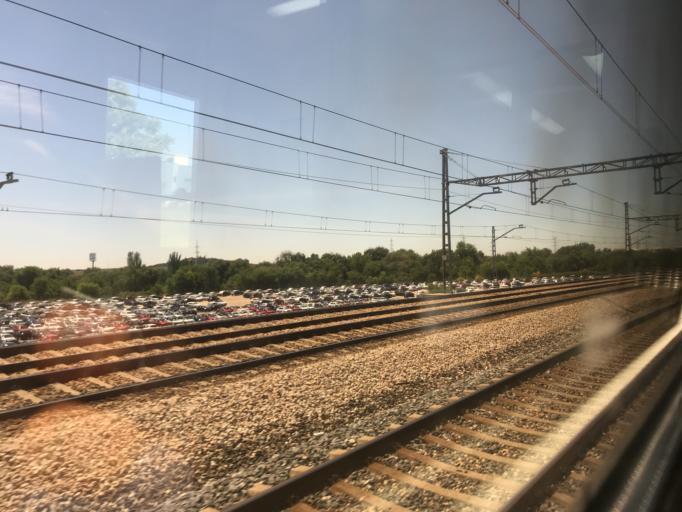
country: ES
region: Madrid
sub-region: Provincia de Madrid
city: Villaverde
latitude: 40.3351
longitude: -3.6866
